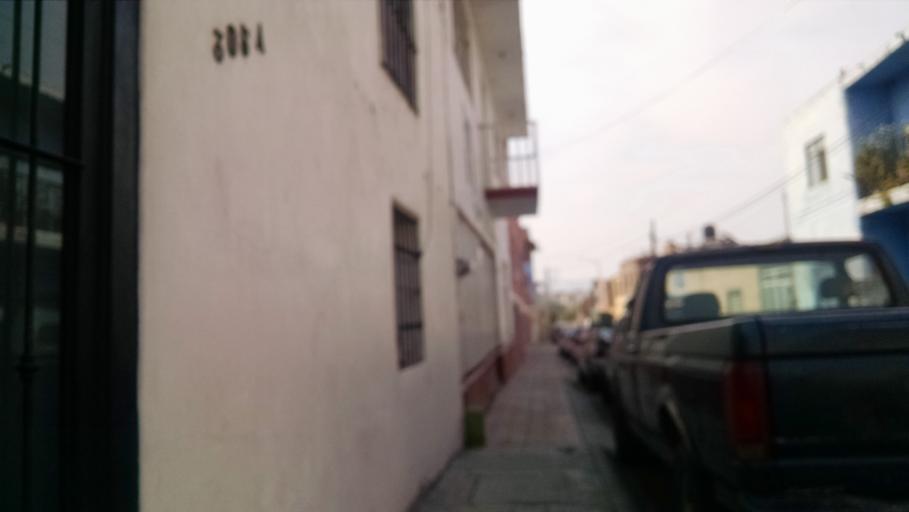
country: MX
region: Aguascalientes
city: Calvillo
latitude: 21.8471
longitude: -102.7153
